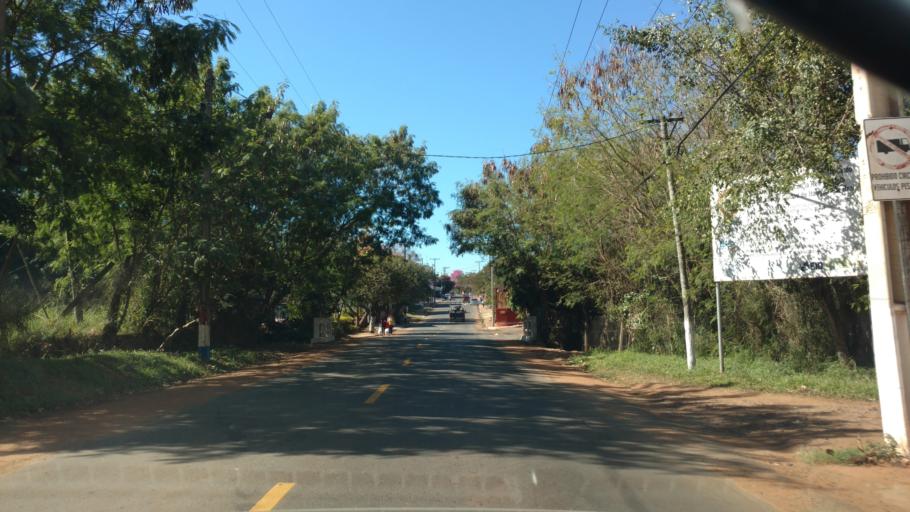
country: PY
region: Central
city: Itaugua
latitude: -25.3903
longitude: -57.3601
